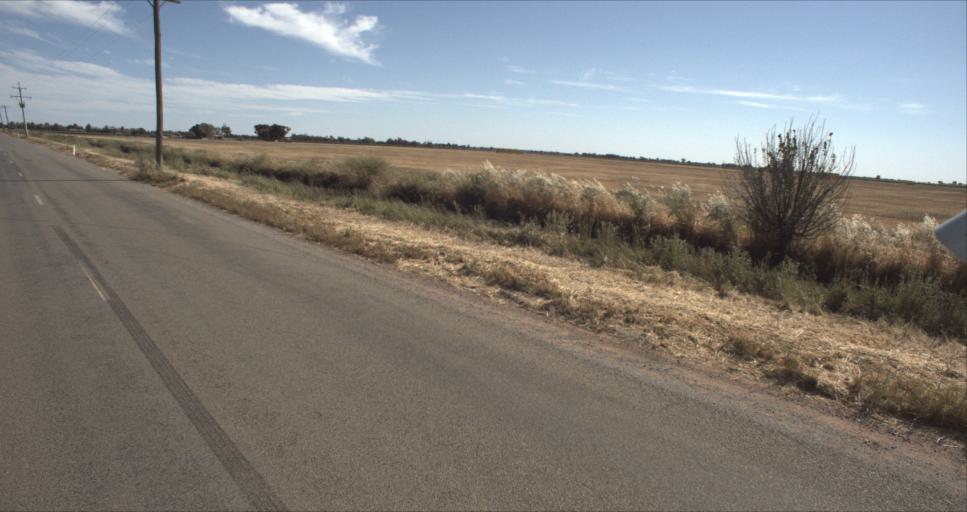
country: AU
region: New South Wales
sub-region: Leeton
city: Leeton
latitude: -34.5726
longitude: 146.3814
